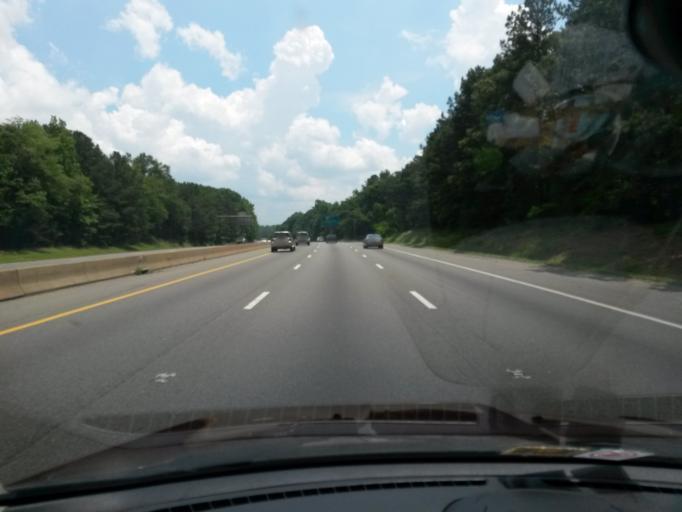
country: US
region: Virginia
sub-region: Chesterfield County
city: Chester
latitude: 37.3867
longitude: -77.4194
